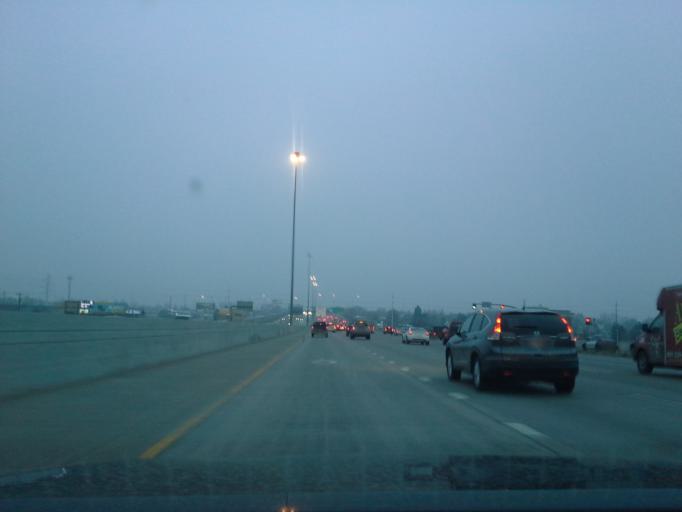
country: US
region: Utah
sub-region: Salt Lake County
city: Murray
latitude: 40.6510
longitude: -111.9022
